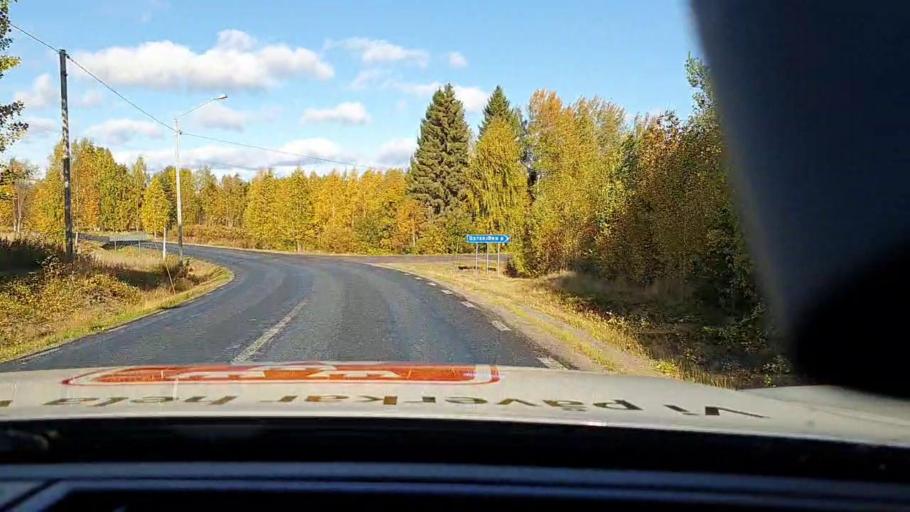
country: SE
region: Vaesterbotten
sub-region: Skelleftea Kommun
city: Langsele
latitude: 65.0045
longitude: 20.0910
